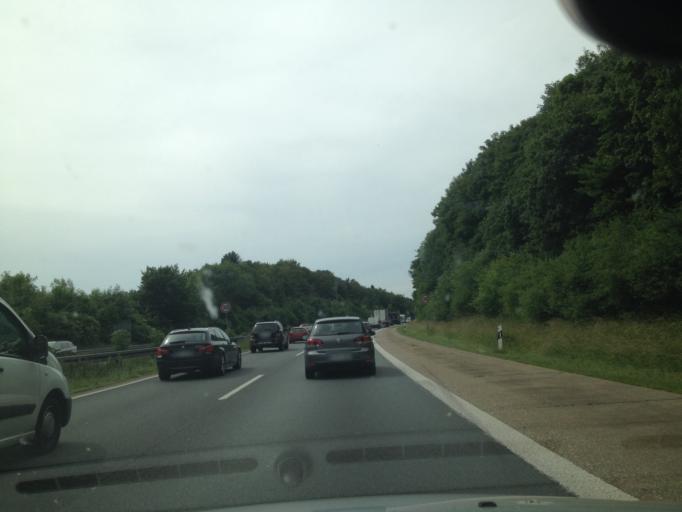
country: DE
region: North Rhine-Westphalia
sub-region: Regierungsbezirk Arnsberg
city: Luedenscheid
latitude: 51.2462
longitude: 7.6271
